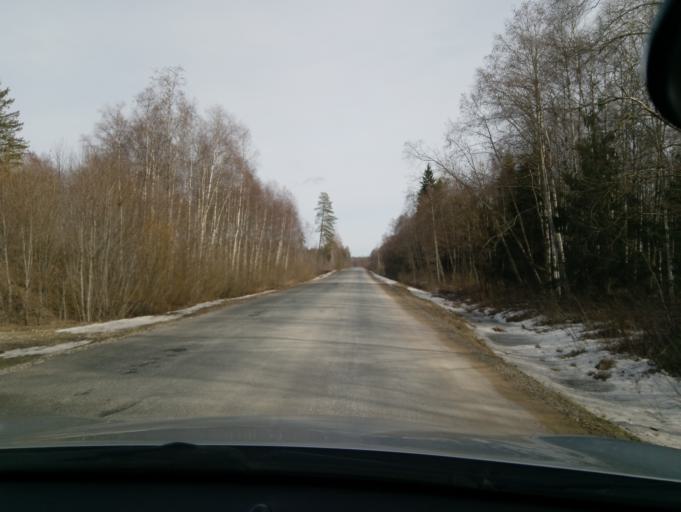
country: EE
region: Jaervamaa
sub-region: Tueri vald
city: Tueri
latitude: 58.8525
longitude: 25.3899
